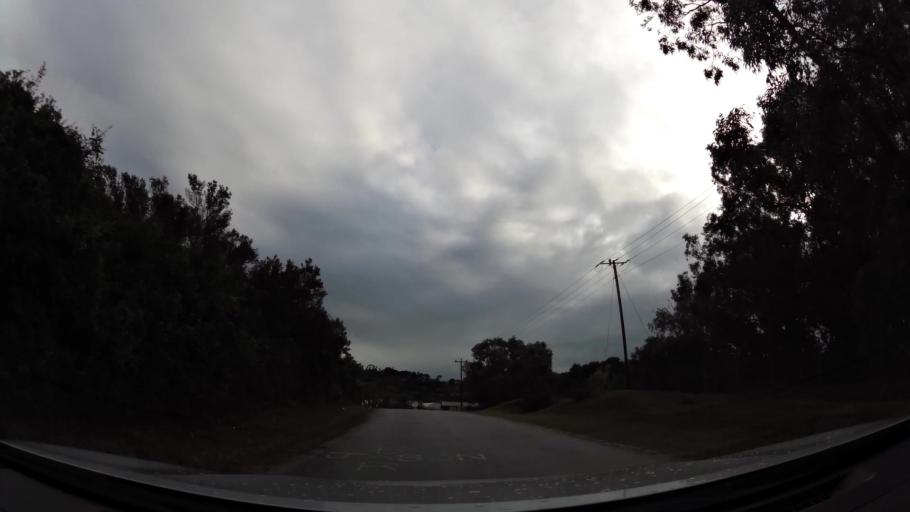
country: ZA
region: Eastern Cape
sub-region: Nelson Mandela Bay Metropolitan Municipality
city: Port Elizabeth
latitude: -34.0139
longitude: 25.4974
